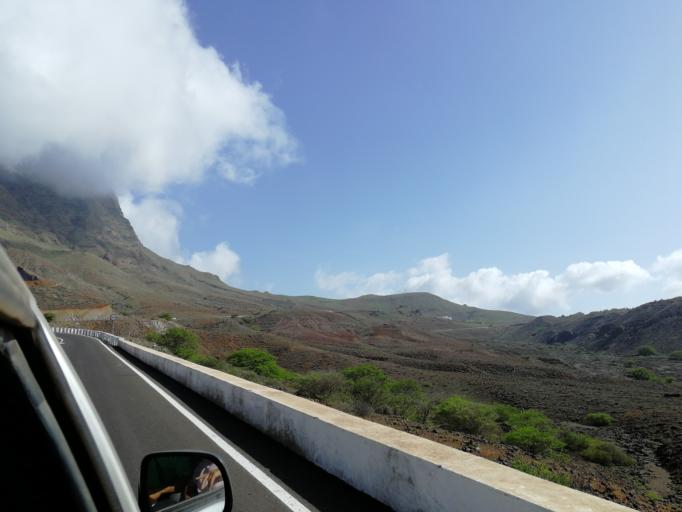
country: CV
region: Sao Vicente
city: Mindelo
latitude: 16.8851
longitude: -24.9412
